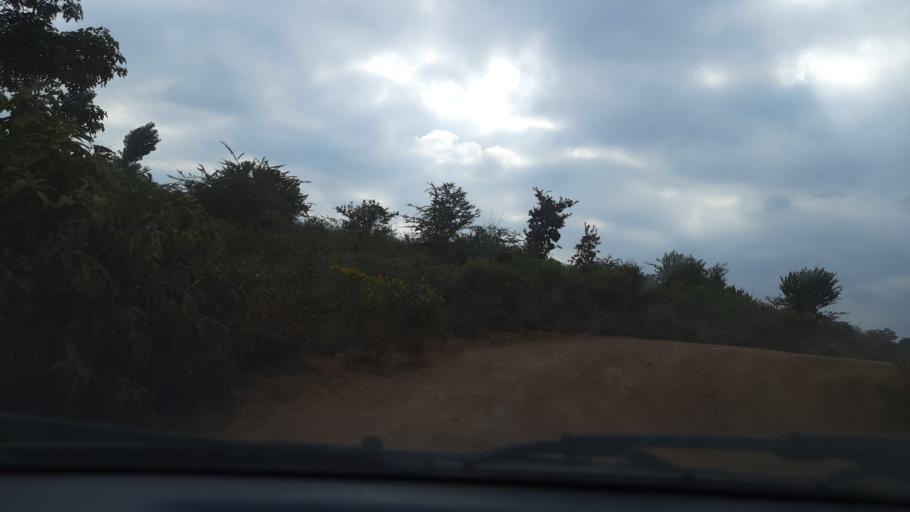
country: TZ
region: Kilimanjaro
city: Moshi
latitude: -2.8695
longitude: 37.3241
